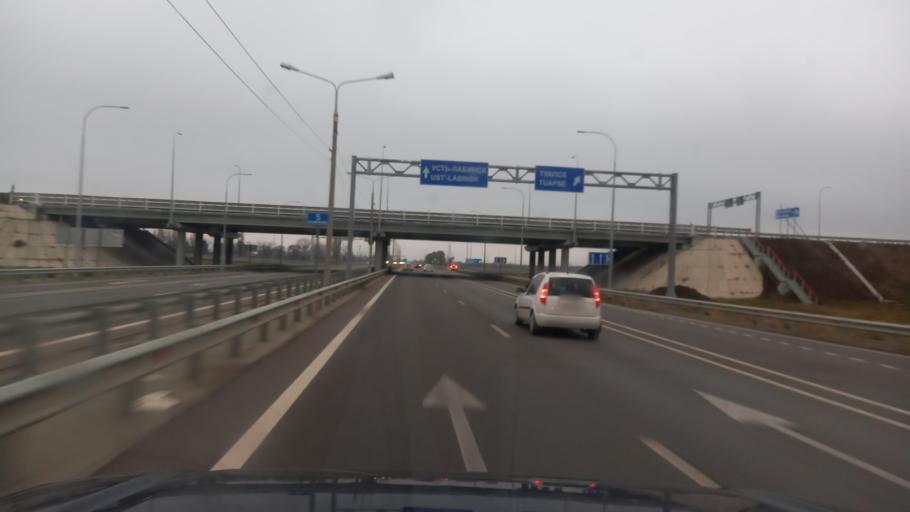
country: RU
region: Adygeya
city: Maykop
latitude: 44.6298
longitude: 40.0440
